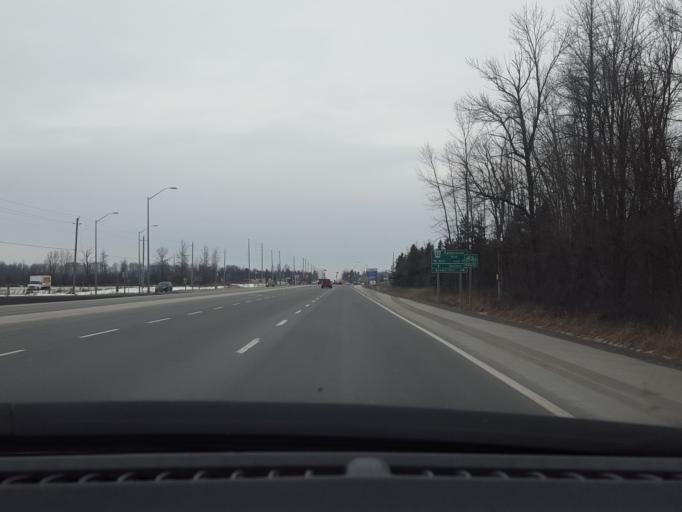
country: CA
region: Ontario
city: Keswick
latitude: 44.1941
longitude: -79.4385
